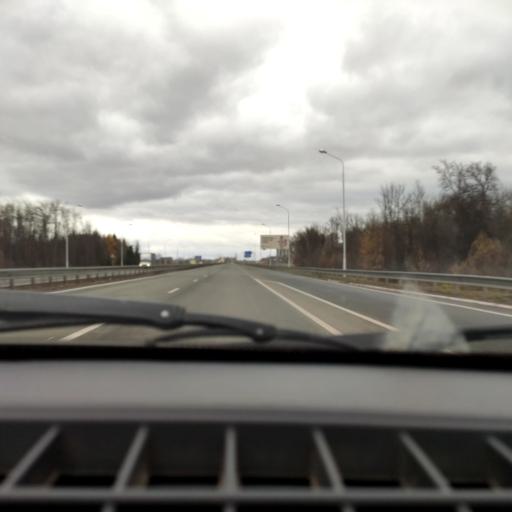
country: RU
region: Bashkortostan
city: Ufa
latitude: 54.6786
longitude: 56.0135
